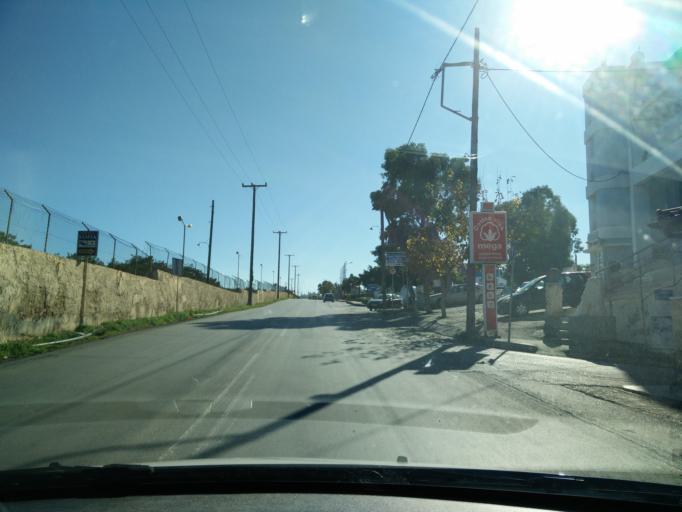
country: GR
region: Crete
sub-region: Nomos Irakleiou
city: Nea Alikarnassos
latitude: 35.3360
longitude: 25.1651
